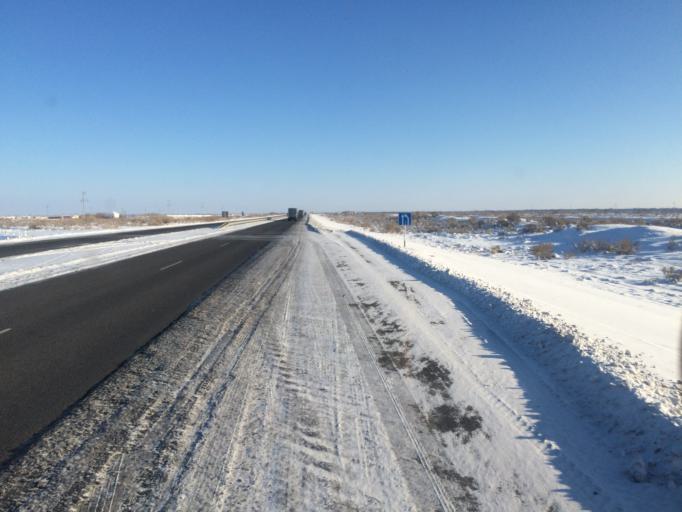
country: KZ
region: Qyzylorda
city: Belkol
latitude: 44.7729
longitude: 65.7647
